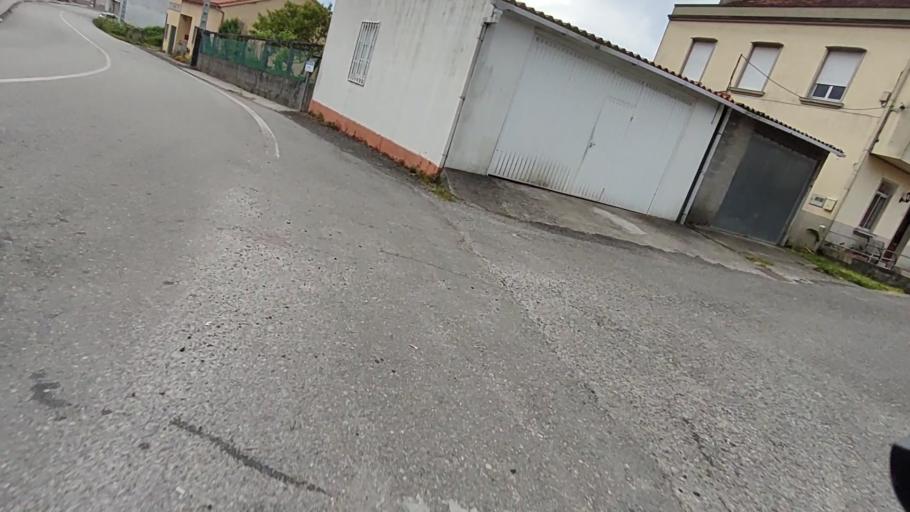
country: ES
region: Galicia
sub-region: Provincia da Coruna
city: Boiro
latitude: 42.6348
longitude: -8.8683
